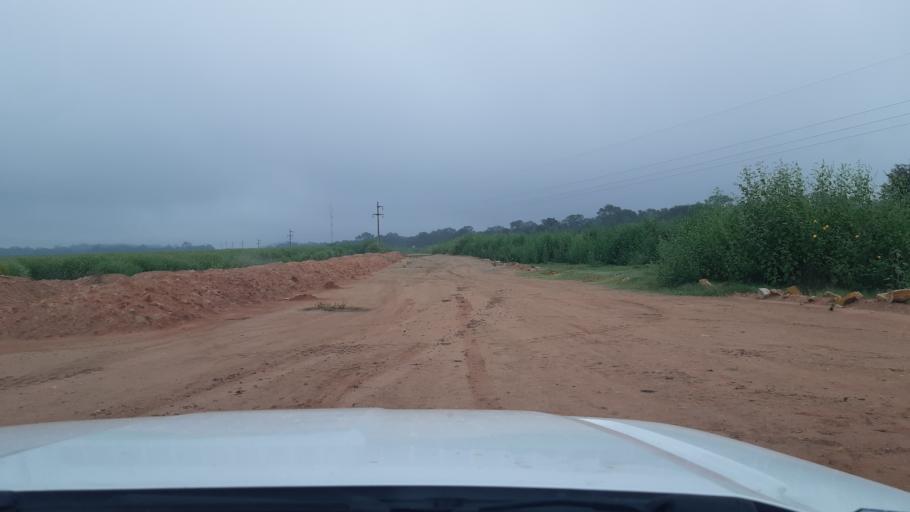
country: AR
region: Jujuy
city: La Mendieta
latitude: -24.3758
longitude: -65.0032
